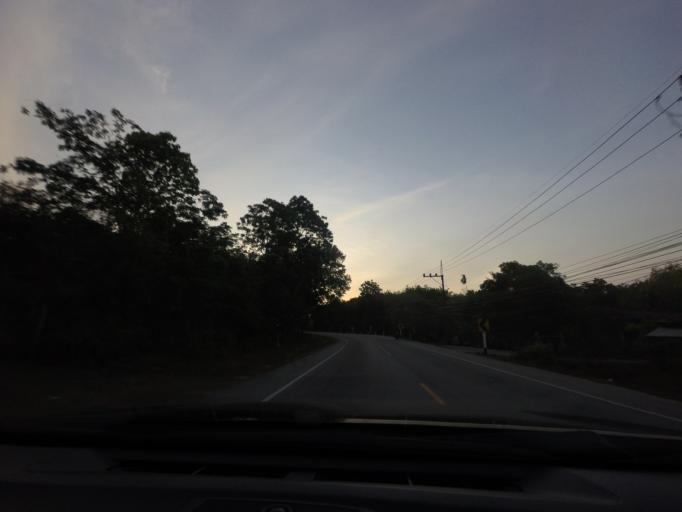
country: TH
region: Narathiwat
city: Rueso
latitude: 6.3554
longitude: 101.5657
